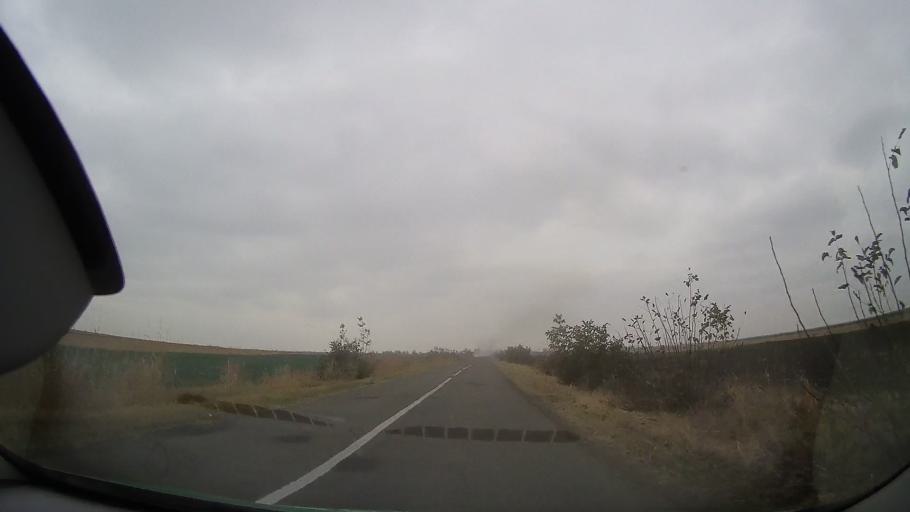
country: RO
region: Ialomita
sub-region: Comuna Valea Macrisului
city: Valea Macrisului
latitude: 44.7617
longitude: 26.7981
